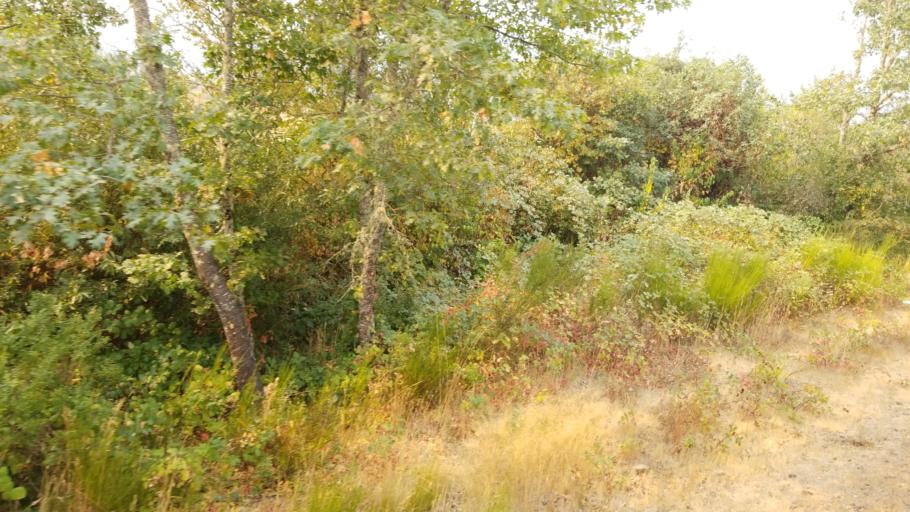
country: US
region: California
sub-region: Mendocino County
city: Willits
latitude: 39.4019
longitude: -123.3560
